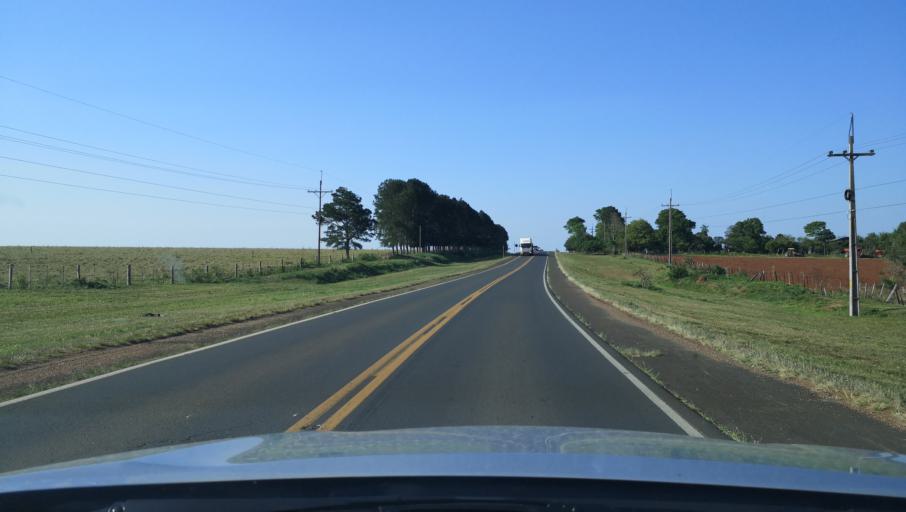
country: PY
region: Misiones
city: Santa Maria
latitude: -26.8433
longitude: -57.0373
